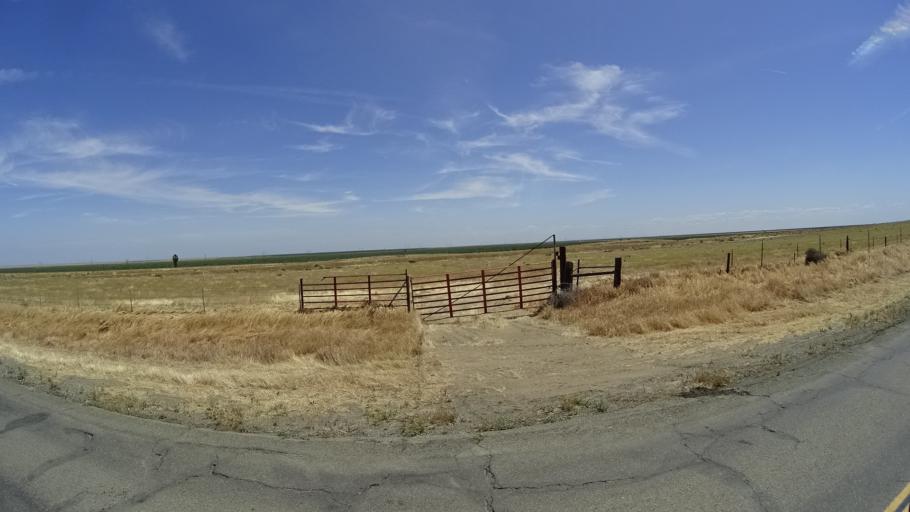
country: US
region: California
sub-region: Kings County
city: Kettleman City
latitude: 35.9033
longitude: -119.9150
